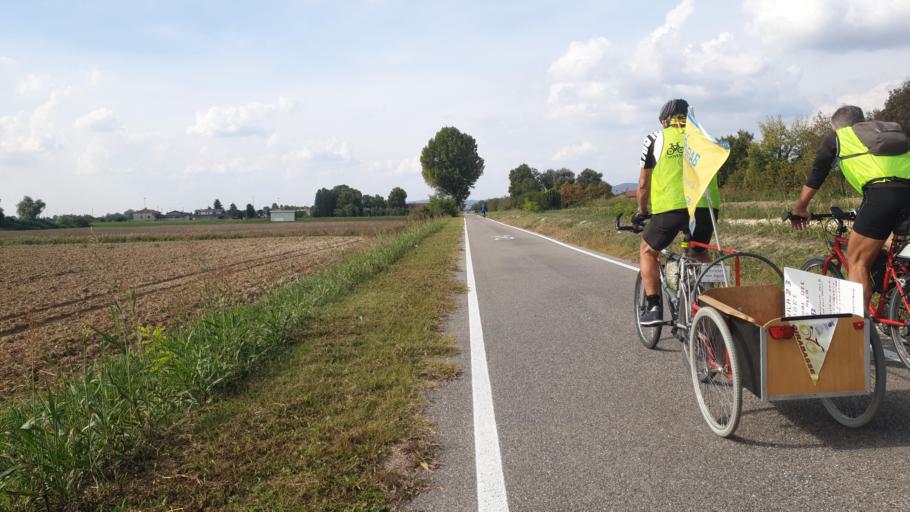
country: IT
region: Veneto
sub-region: Provincia di Vicenza
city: Agugliaro
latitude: 45.3285
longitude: 11.5797
